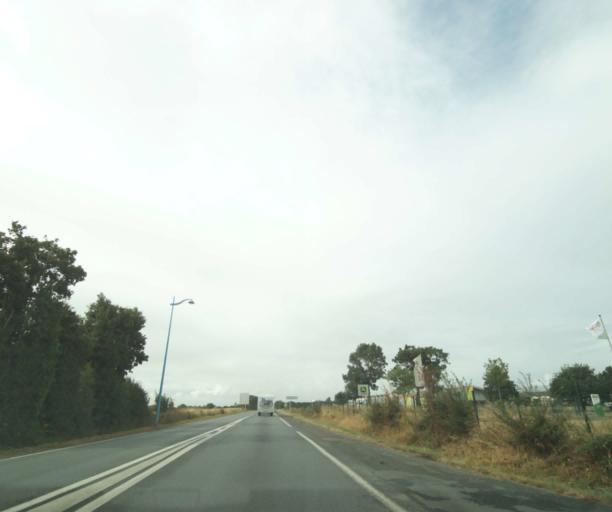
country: FR
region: Pays de la Loire
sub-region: Departement de la Vendee
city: Sainte-Gemme-la-Plaine
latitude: 46.4667
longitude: -1.1086
